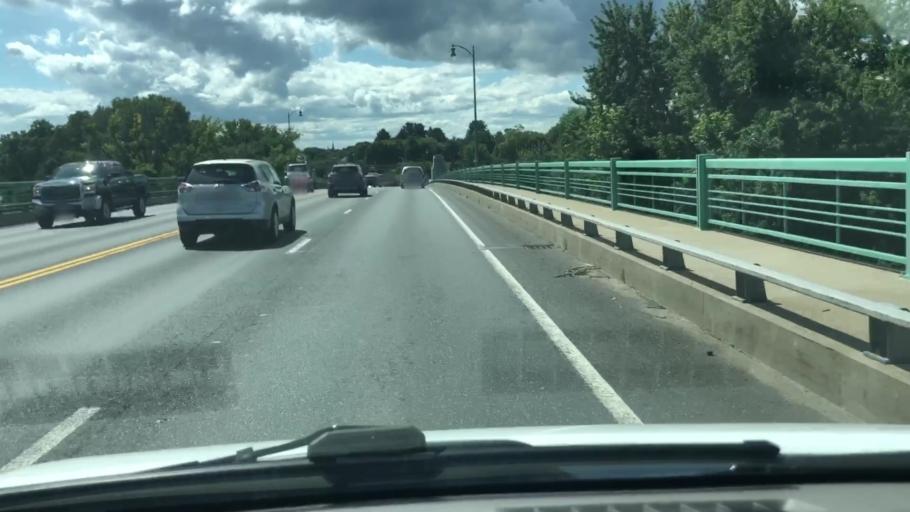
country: US
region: Massachusetts
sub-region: Hampshire County
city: Northampton
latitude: 42.3358
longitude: -72.6186
